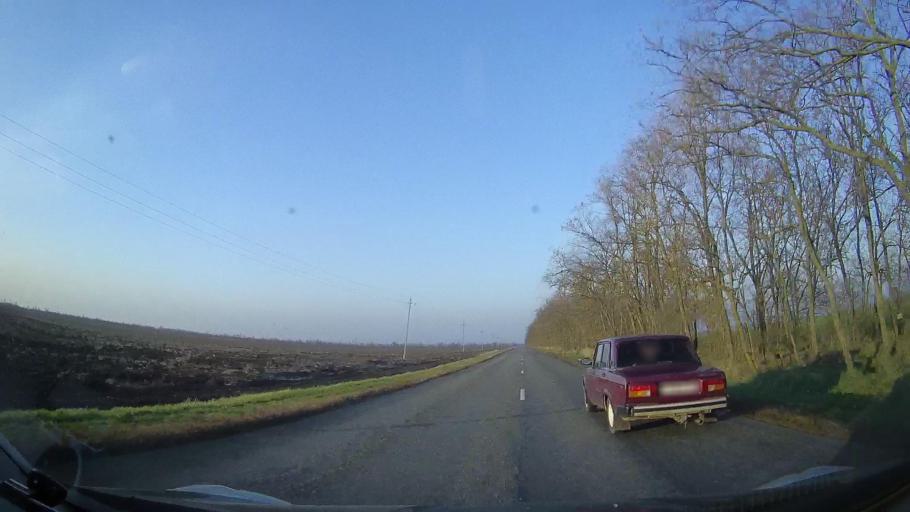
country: RU
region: Rostov
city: Ol'ginskaya
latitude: 47.0903
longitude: 39.9775
